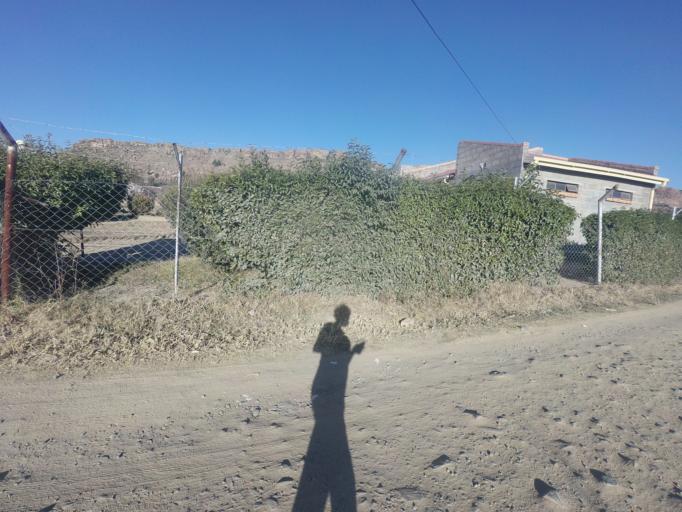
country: LS
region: Maseru
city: Maseru
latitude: -29.3001
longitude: 27.5470
